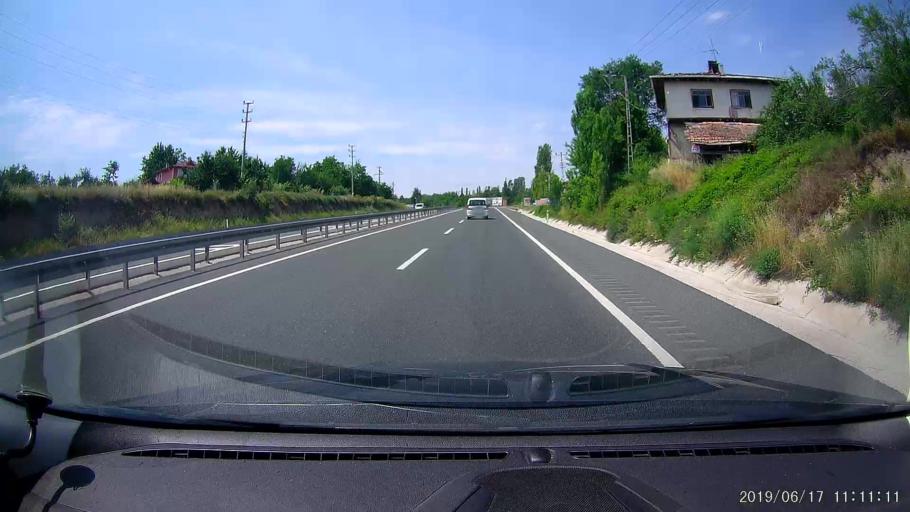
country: TR
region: Kastamonu
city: Tosya
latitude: 40.9899
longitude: 34.0126
